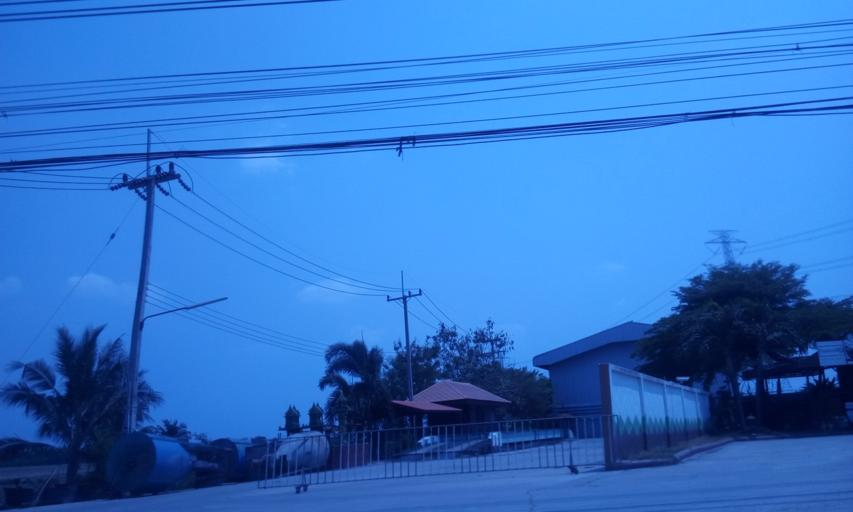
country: TH
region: Chachoengsao
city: Bang Nam Priao
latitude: 13.8269
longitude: 101.0552
